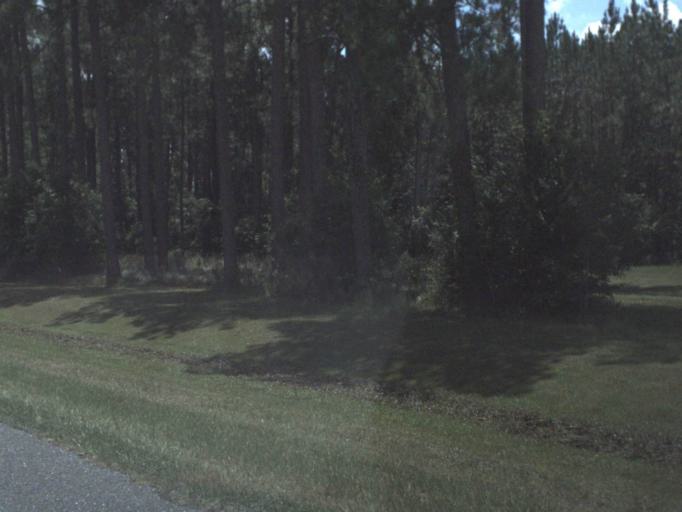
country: US
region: Florida
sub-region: Bradford County
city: Starke
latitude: 30.0447
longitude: -82.1689
